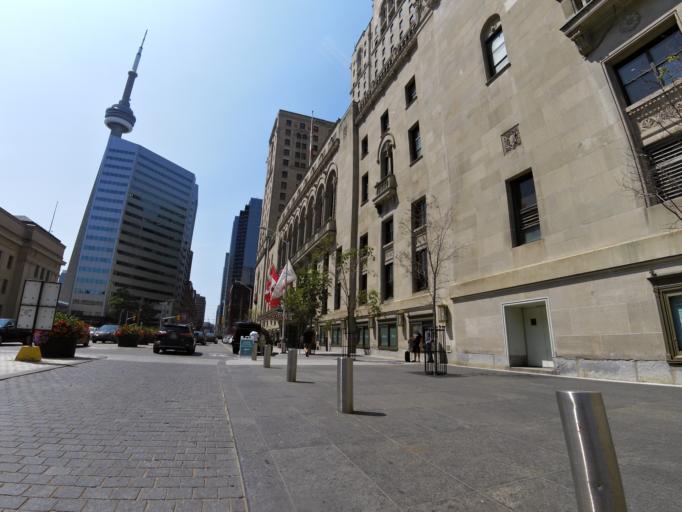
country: CA
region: Ontario
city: Toronto
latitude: 43.6463
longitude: -79.3807
